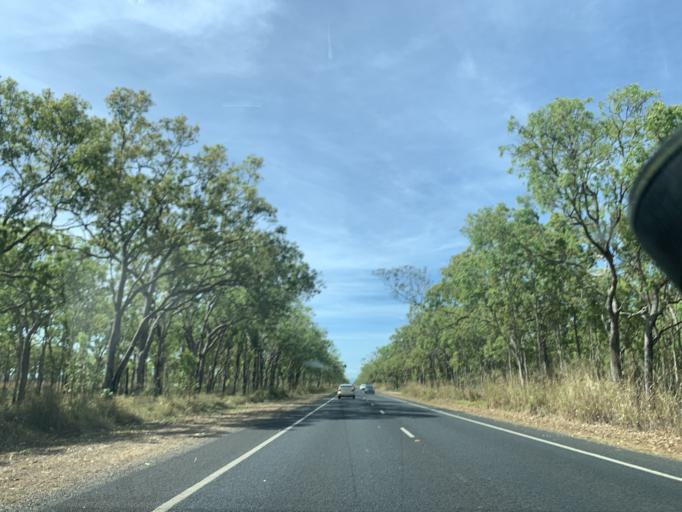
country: AU
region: Queensland
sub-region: Tablelands
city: Mareeba
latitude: -17.0434
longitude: 145.4300
